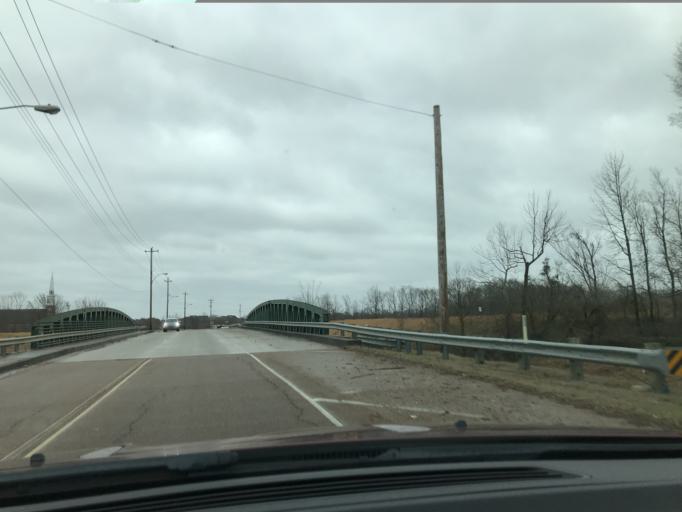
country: US
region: Tennessee
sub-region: Shelby County
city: Collierville
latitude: 35.0908
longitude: -89.7115
